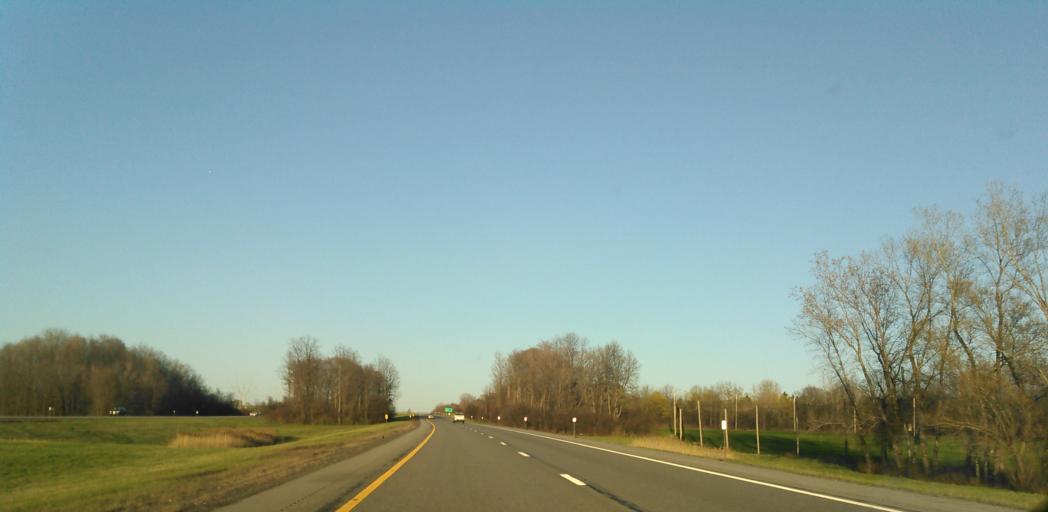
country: US
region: New York
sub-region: Monroe County
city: Honeoye Falls
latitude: 43.0467
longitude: -77.6123
